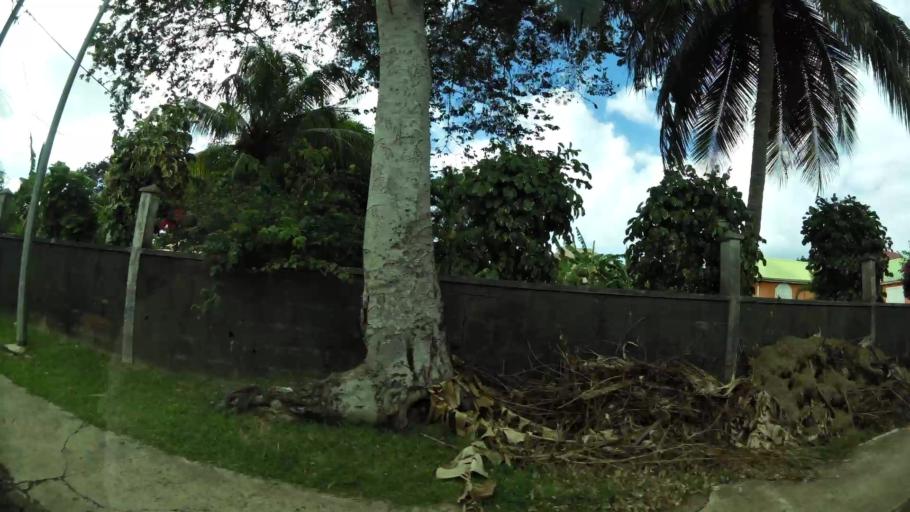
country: GP
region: Guadeloupe
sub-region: Guadeloupe
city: Sainte-Rose
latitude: 16.3265
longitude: -61.7010
